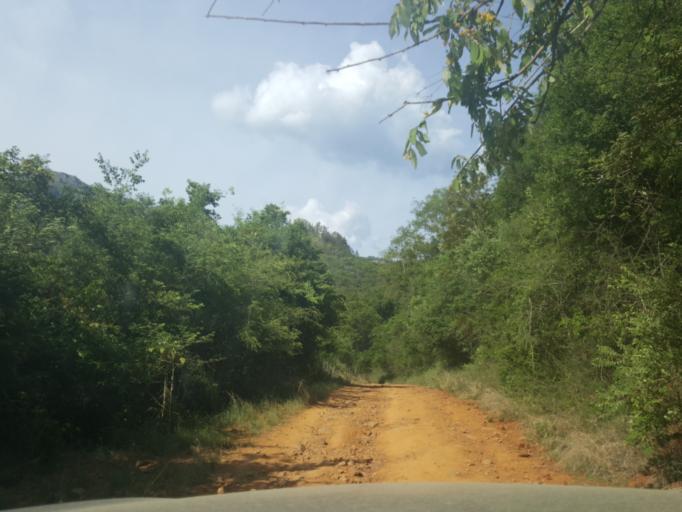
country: ZA
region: Limpopo
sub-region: Mopani District Municipality
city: Hoedspruit
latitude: -24.5926
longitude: 30.8282
